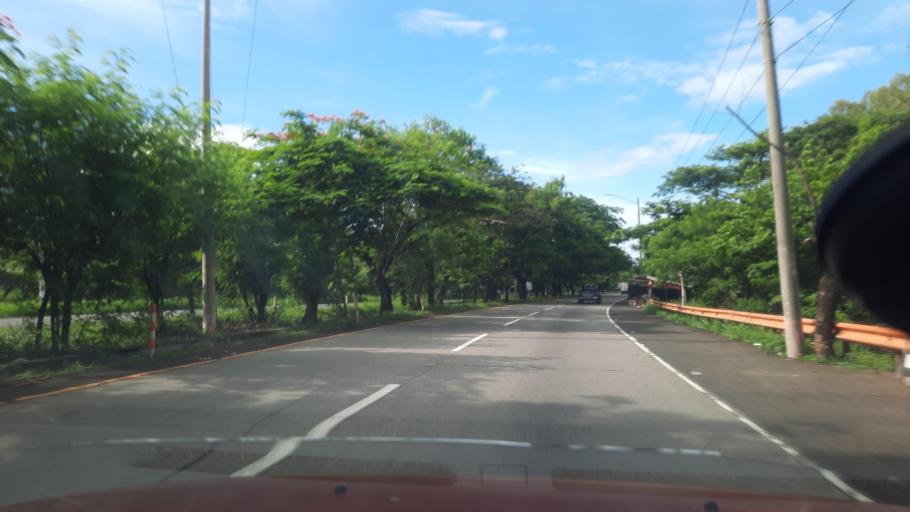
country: SV
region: La Paz
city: El Rosario
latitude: 13.4894
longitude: -89.0667
